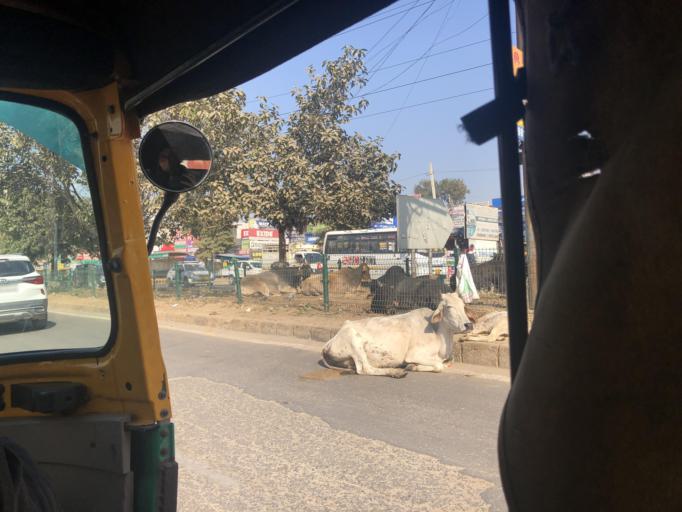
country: IN
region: Haryana
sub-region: Gurgaon
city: Gurgaon
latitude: 28.4393
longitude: 77.0887
